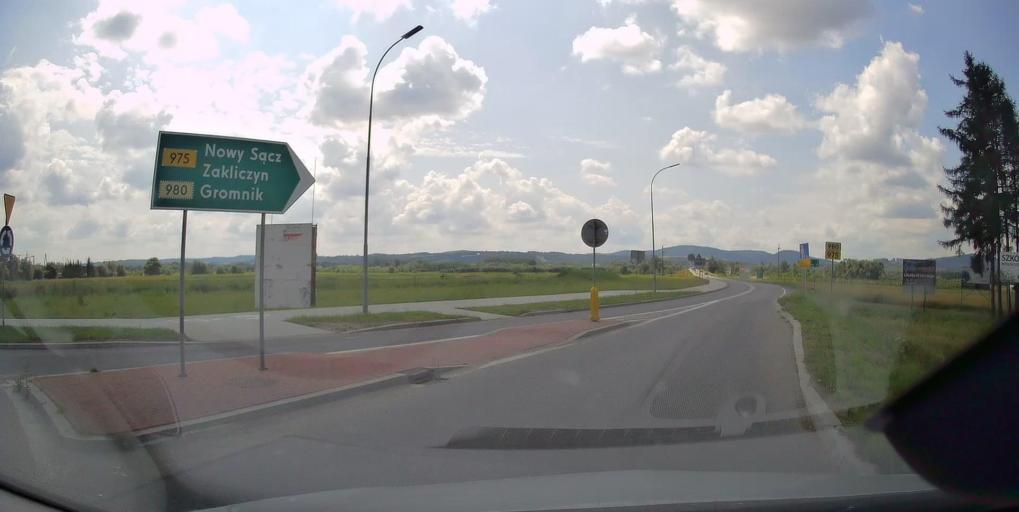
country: PL
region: Lesser Poland Voivodeship
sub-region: Powiat tarnowski
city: Zakliczyn
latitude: 49.8718
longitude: 20.8109
